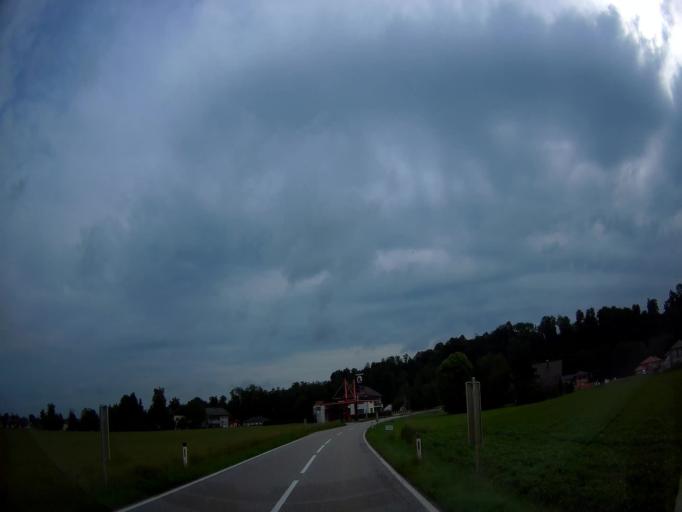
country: AT
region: Upper Austria
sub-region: Politischer Bezirk Braunau am Inn
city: Braunau am Inn
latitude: 48.1825
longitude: 13.1308
